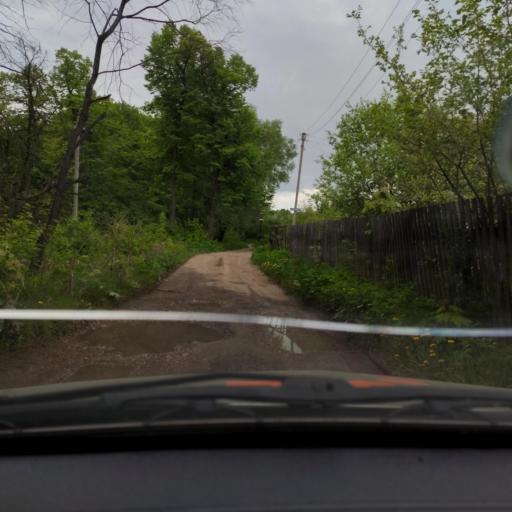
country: RU
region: Bashkortostan
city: Blagoveshchensk
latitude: 54.9403
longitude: 56.0869
